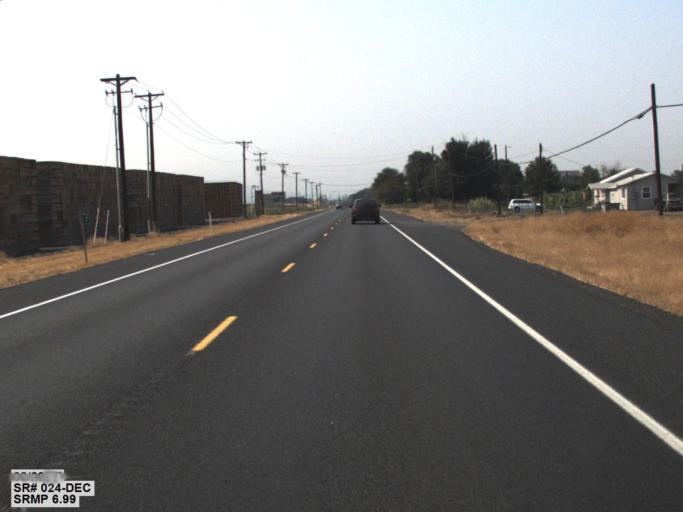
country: US
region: Washington
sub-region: Yakima County
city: Terrace Heights
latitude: 46.5496
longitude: -120.3463
